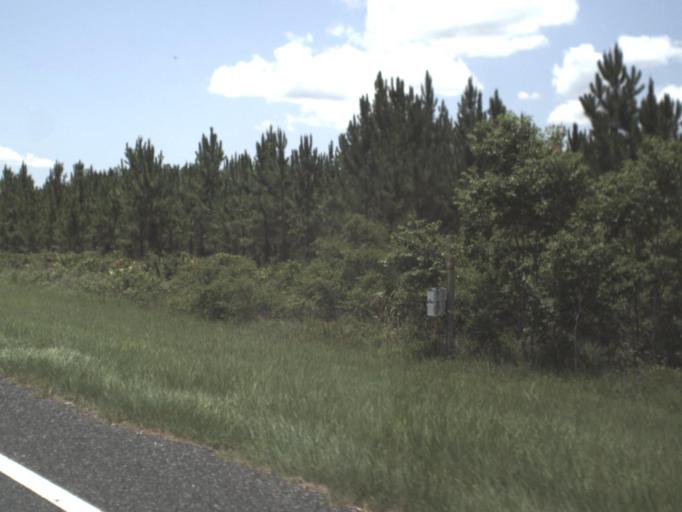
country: US
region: Florida
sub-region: Taylor County
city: Steinhatchee
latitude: 29.7645
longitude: -83.3226
